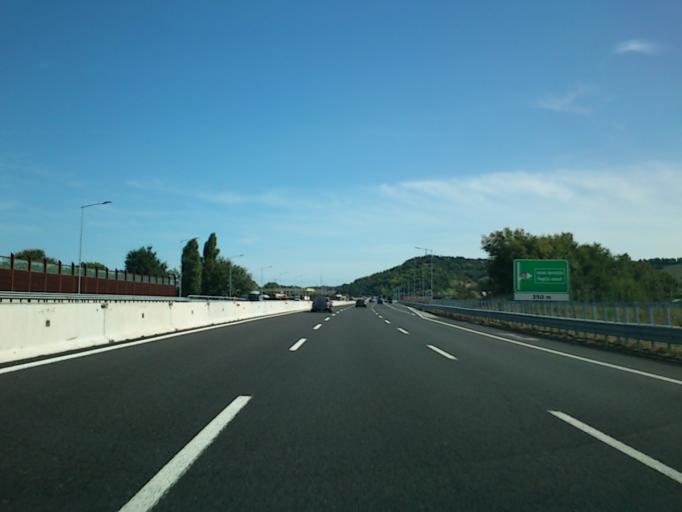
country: IT
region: The Marches
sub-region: Provincia di Pesaro e Urbino
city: Pesaro
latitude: 43.8965
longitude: 12.8747
